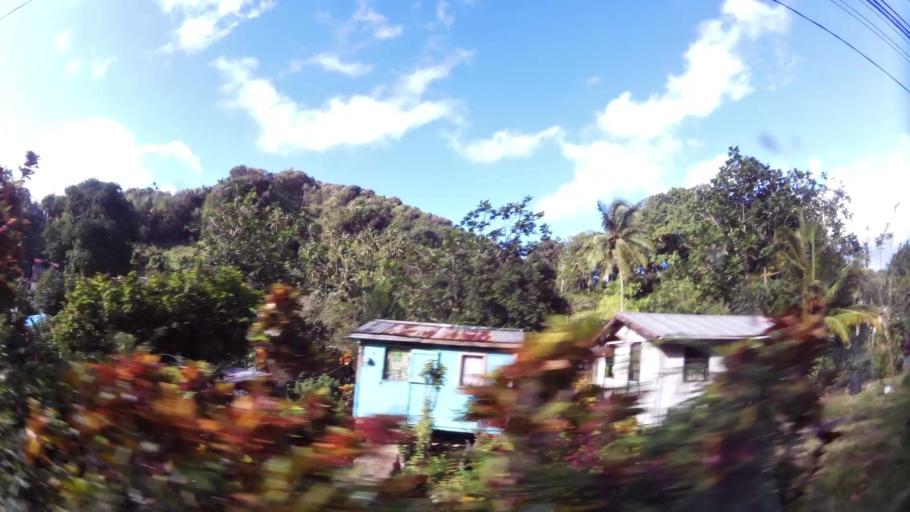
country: DM
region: Saint John
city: Portsmouth
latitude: 15.5843
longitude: -61.4114
